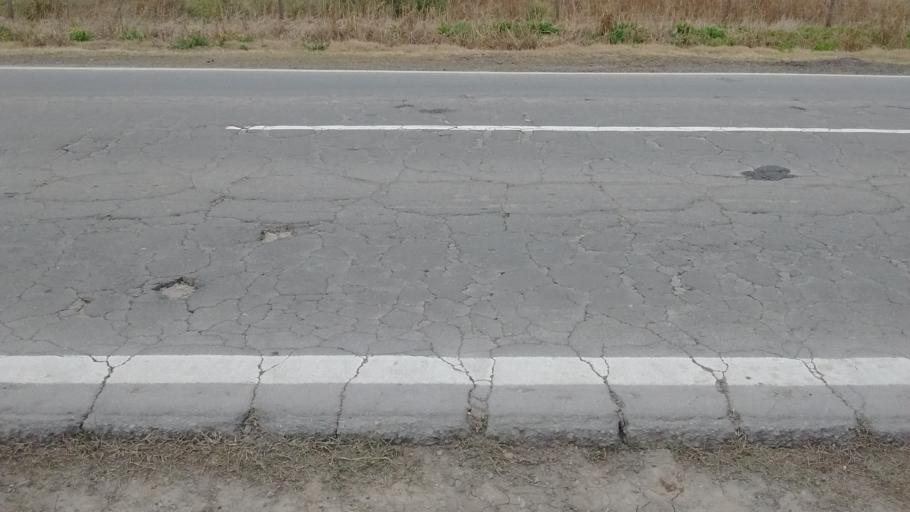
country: AR
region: Santa Fe
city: Las Rosas
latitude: -32.5707
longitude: -61.5488
